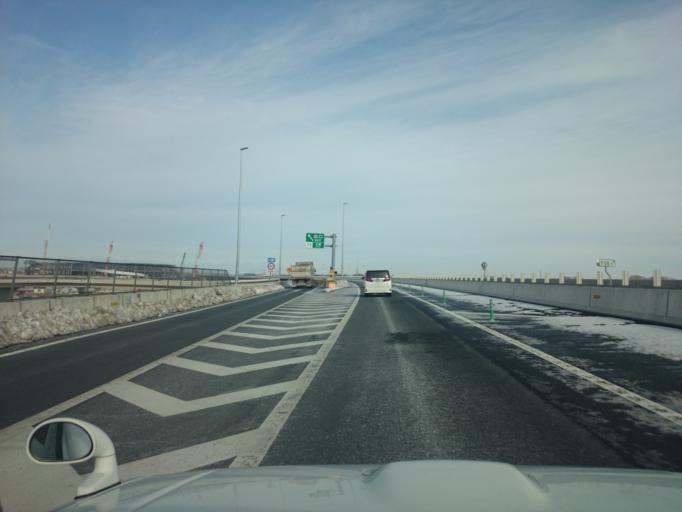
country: JP
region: Ibaraki
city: Sakai
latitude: 36.0932
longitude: 139.7619
